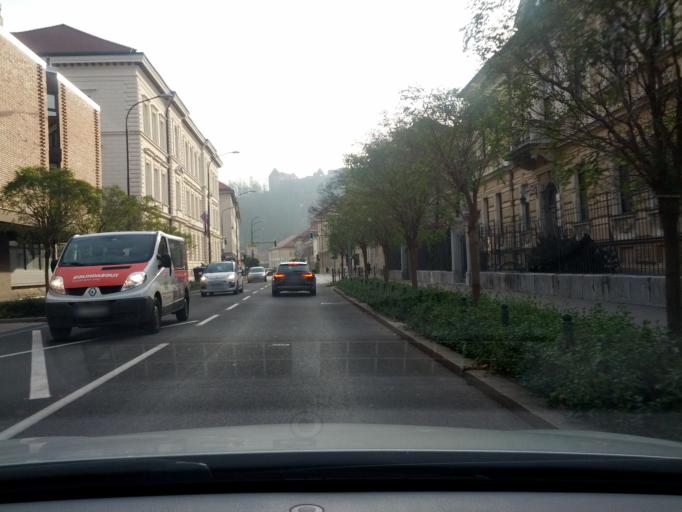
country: SI
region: Ljubljana
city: Ljubljana
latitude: 46.0546
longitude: 14.5109
